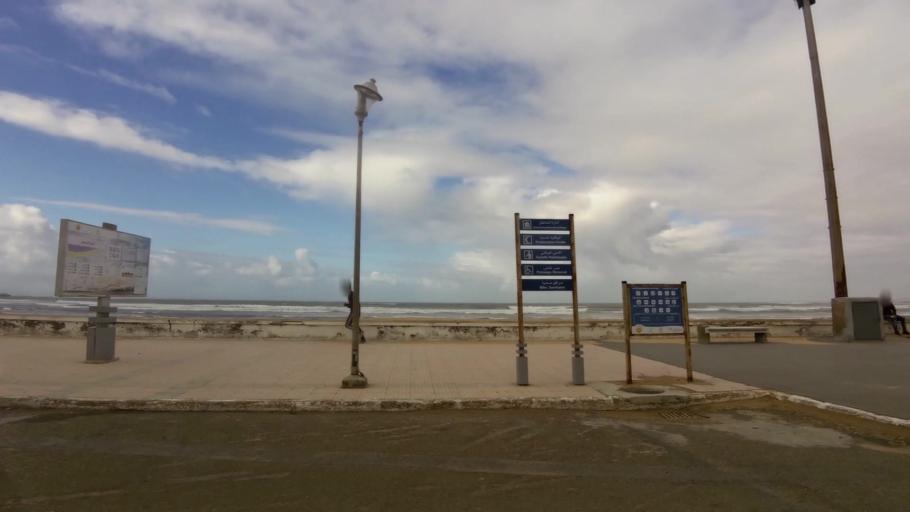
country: MA
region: Doukkala-Abda
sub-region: El-Jadida
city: El Jadida
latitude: 33.2447
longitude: -8.4890
